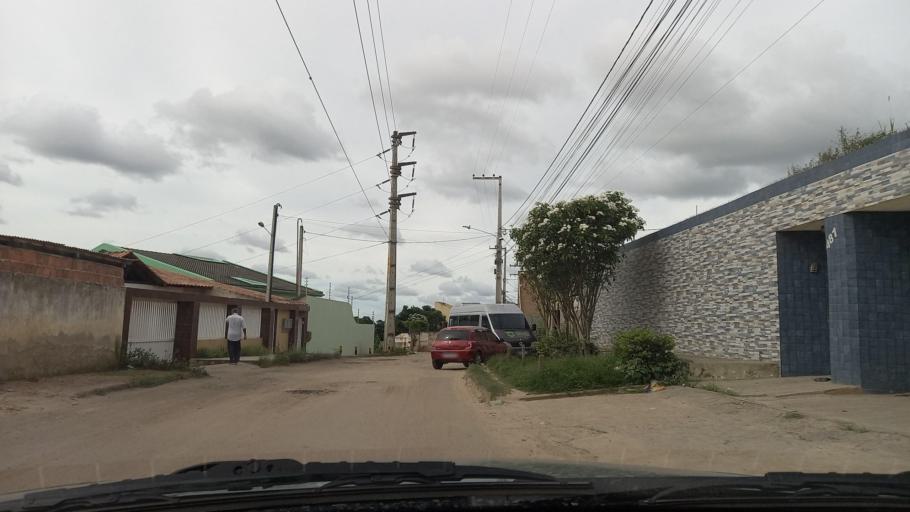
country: BR
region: Pernambuco
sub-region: Gravata
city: Gravata
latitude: -8.2098
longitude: -35.5758
